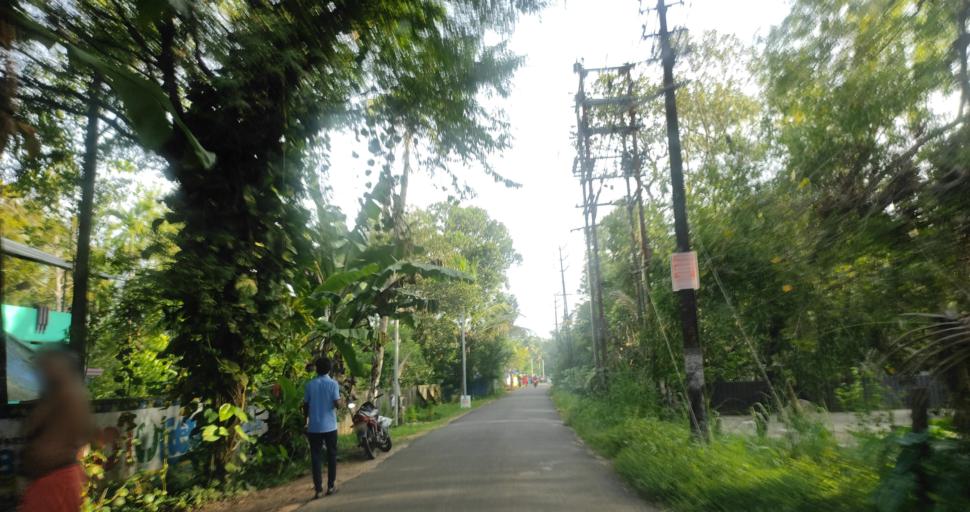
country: IN
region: Kerala
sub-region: Alappuzha
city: Shertallai
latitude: 9.6428
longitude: 76.3446
